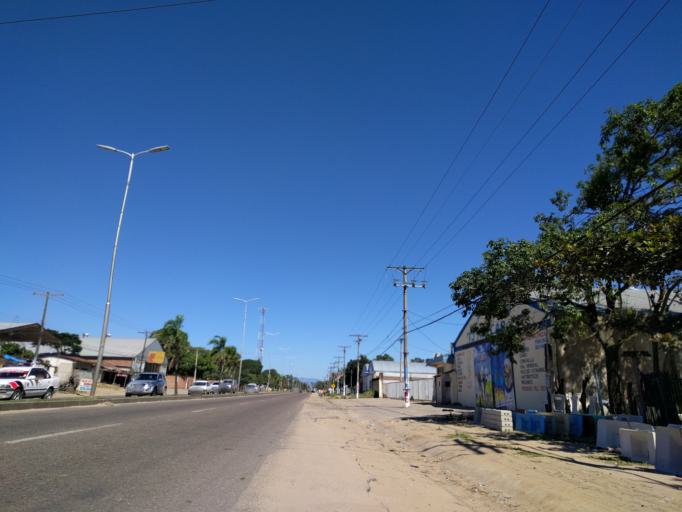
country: BO
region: Santa Cruz
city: Santa Cruz de la Sierra
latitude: -17.8506
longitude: -63.2522
